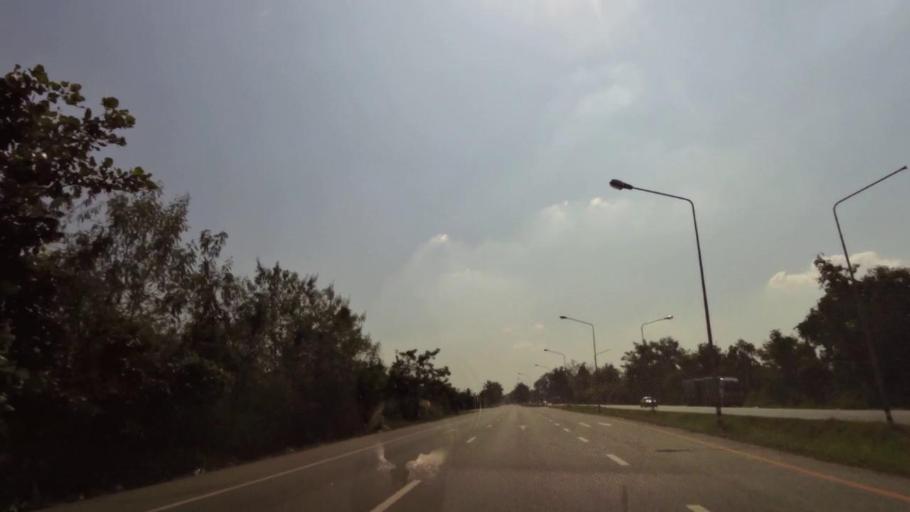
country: TH
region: Phichit
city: Bueng Na Rang
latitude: 16.2438
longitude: 100.1253
